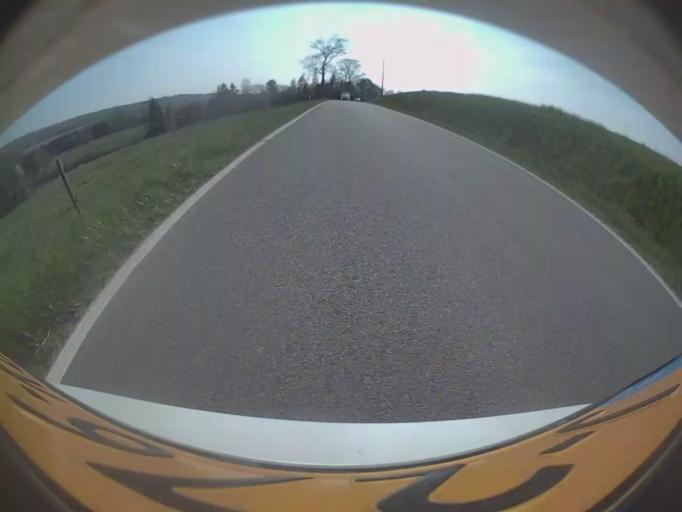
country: BE
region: Wallonia
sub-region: Province de Namur
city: Havelange
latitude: 50.3316
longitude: 5.2750
